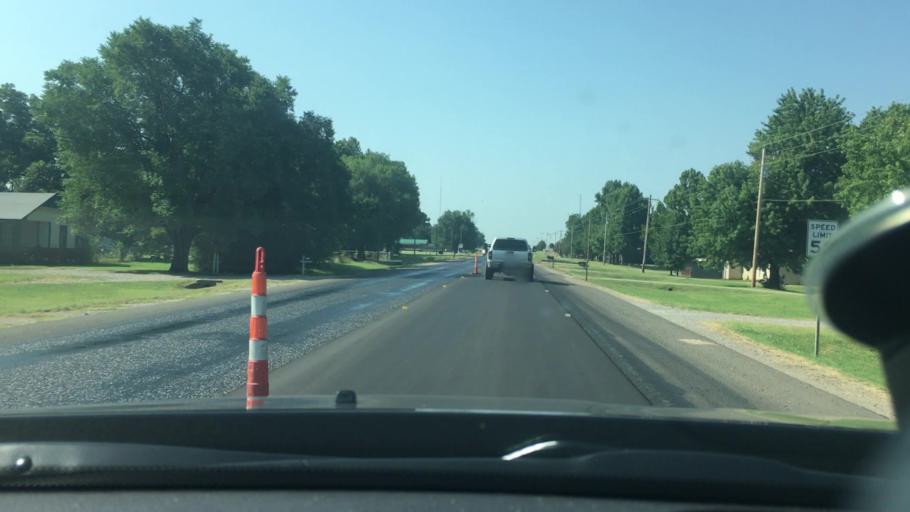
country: US
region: Oklahoma
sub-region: Garvin County
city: Lindsay
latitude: 34.8090
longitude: -97.5983
